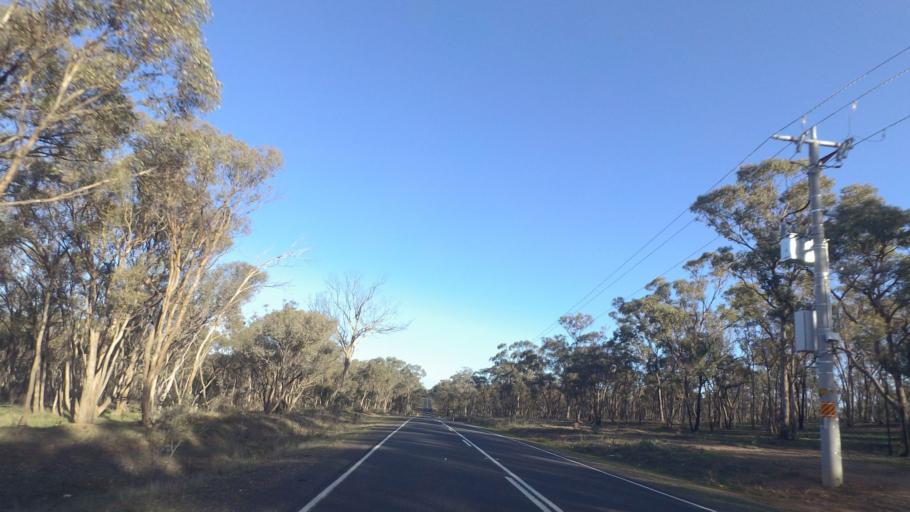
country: AU
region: Victoria
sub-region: Greater Bendigo
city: Kennington
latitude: -36.8840
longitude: 144.4930
